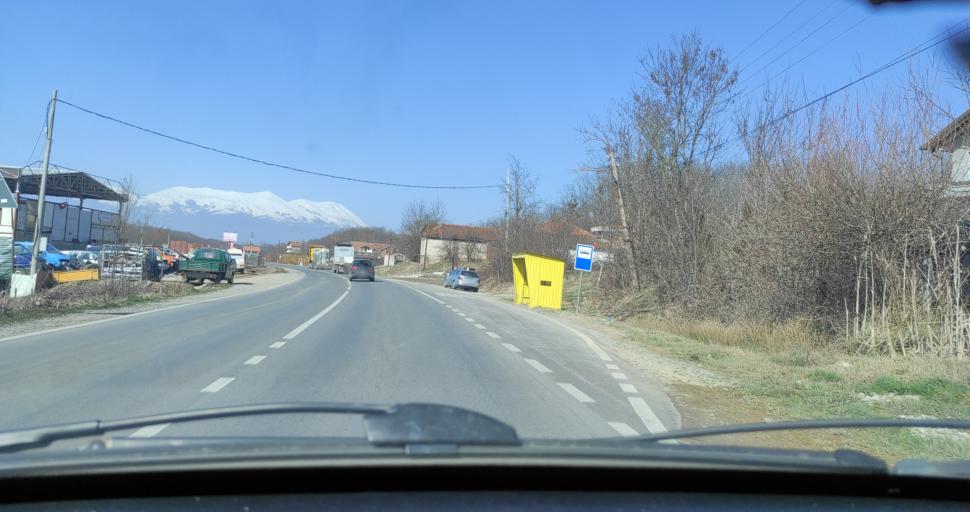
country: XK
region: Pec
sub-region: Komuna e Pejes
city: Kosuriq
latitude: 42.6352
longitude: 20.4470
